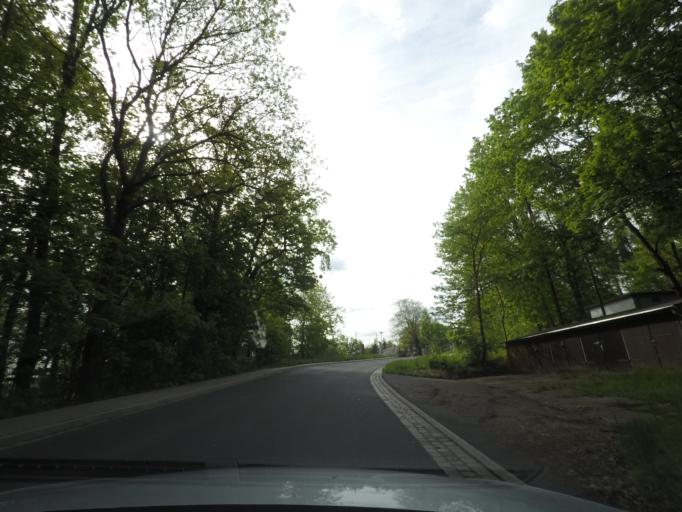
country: DE
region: Saxony
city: Dobeln
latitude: 51.1126
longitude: 13.1160
